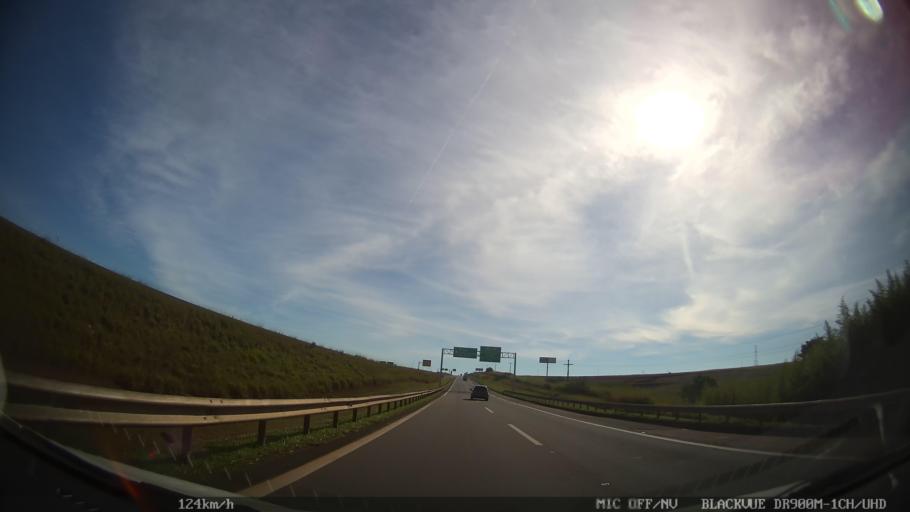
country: BR
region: Sao Paulo
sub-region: Cordeiropolis
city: Cordeiropolis
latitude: -22.4808
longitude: -47.3992
